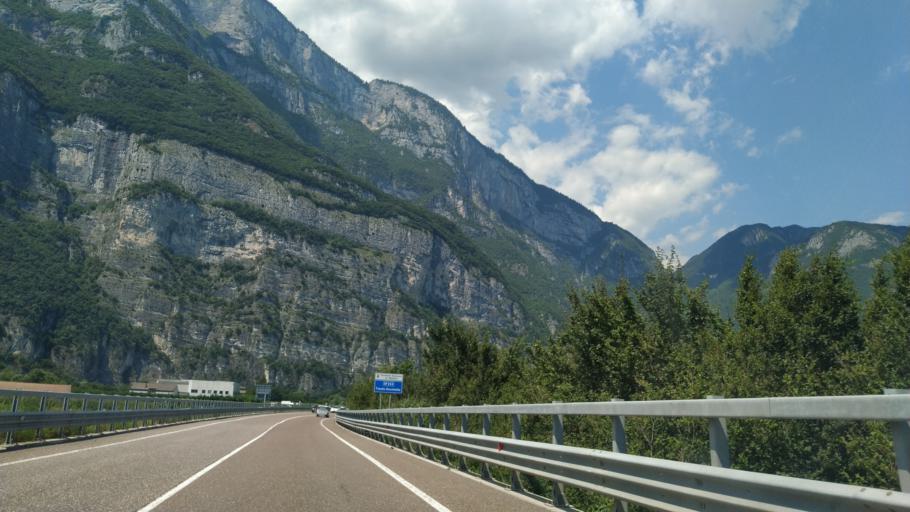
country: IT
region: Trentino-Alto Adige
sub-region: Provincia di Trento
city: Zambana
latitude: 46.1410
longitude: 11.0824
